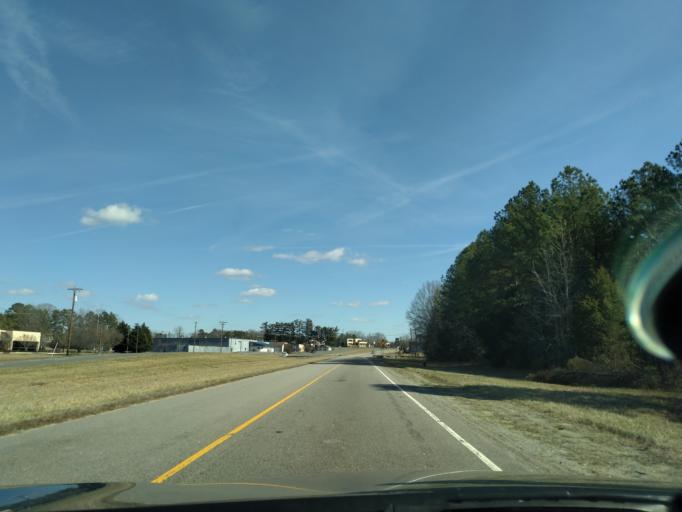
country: US
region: Virginia
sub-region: Nottoway County
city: Crewe
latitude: 37.1903
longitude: -78.1536
